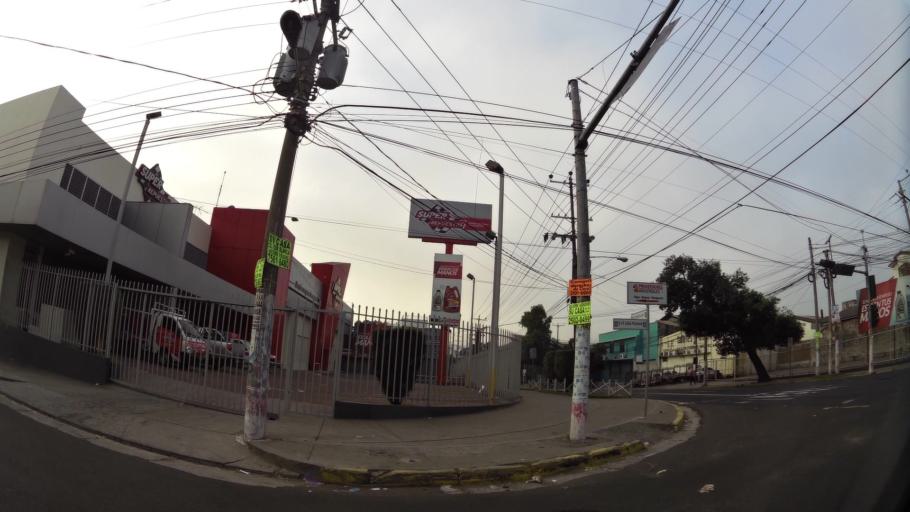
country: SV
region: San Salvador
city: San Salvador
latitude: 13.6977
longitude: -89.2050
